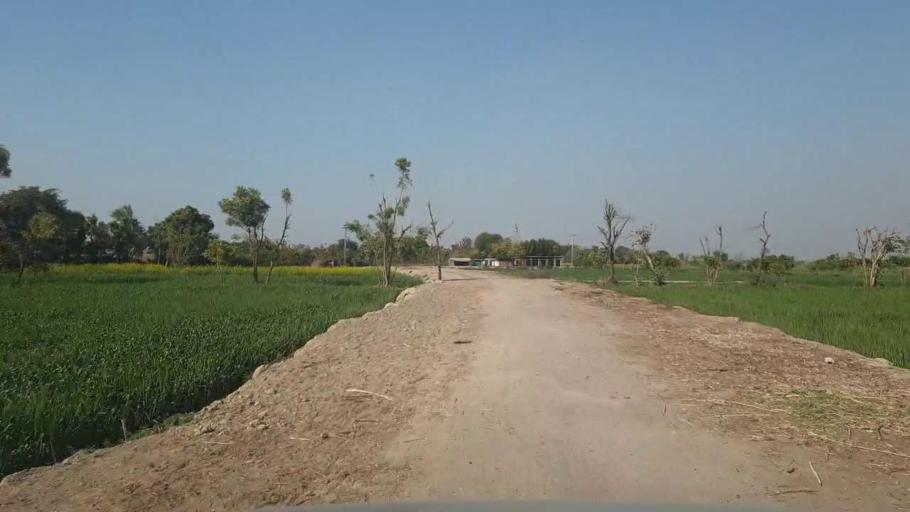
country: PK
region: Sindh
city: Chambar
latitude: 25.3258
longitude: 68.8526
